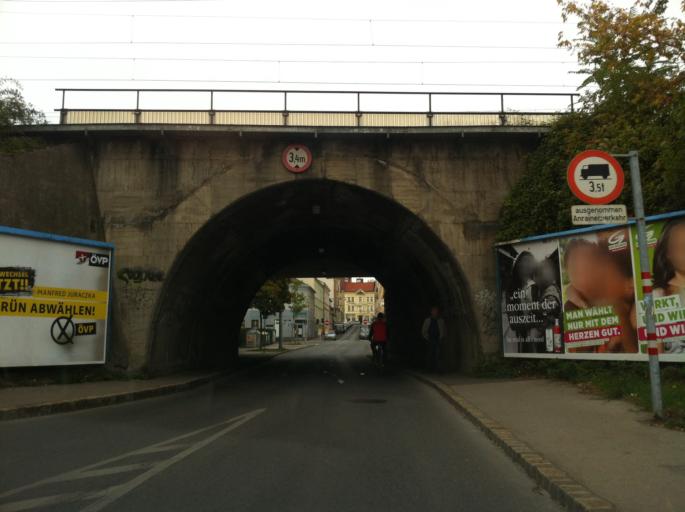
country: AT
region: Lower Austria
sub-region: Politischer Bezirk Modling
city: Perchtoldsdorf
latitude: 48.1932
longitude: 16.2812
